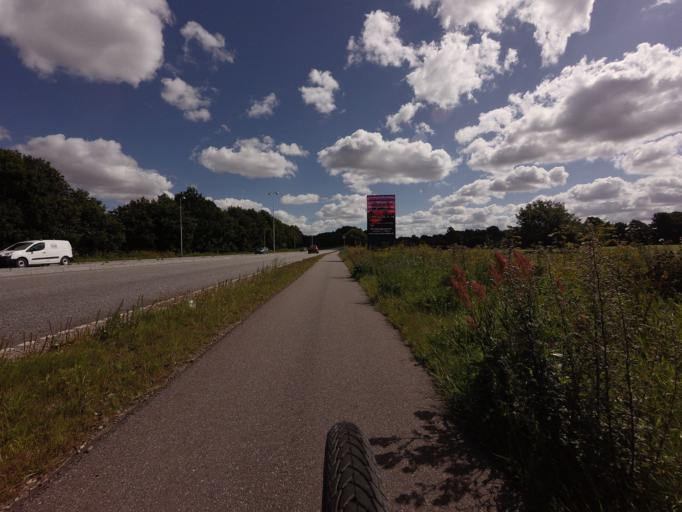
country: DK
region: Central Jutland
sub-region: Horsens Kommune
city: Horsens
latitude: 55.8774
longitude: 9.8109
